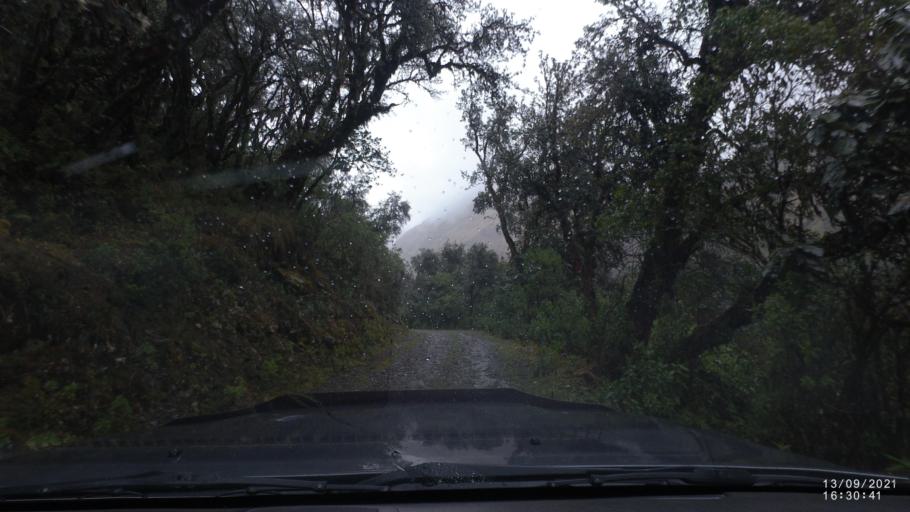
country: BO
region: Cochabamba
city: Colomi
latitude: -17.2746
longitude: -65.7115
